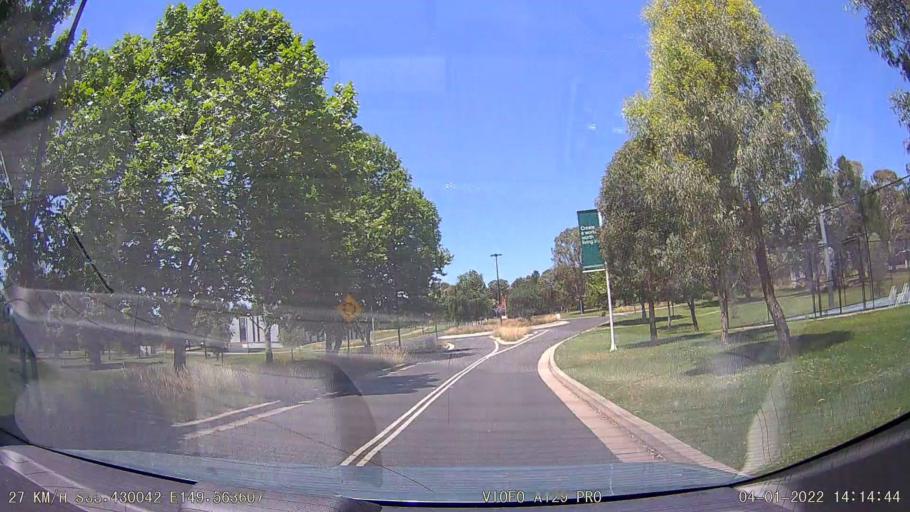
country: AU
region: New South Wales
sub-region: Bathurst Regional
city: Bathurst
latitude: -33.4301
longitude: 149.5636
